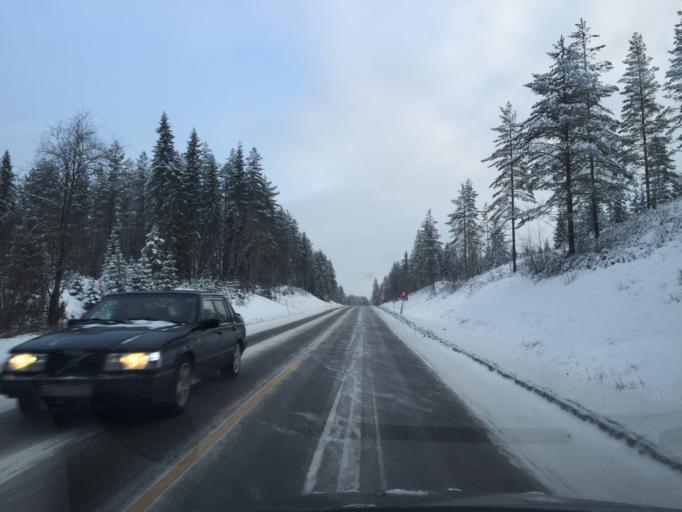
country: NO
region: Hedmark
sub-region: Elverum
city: Elverum
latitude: 60.9587
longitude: 11.7076
